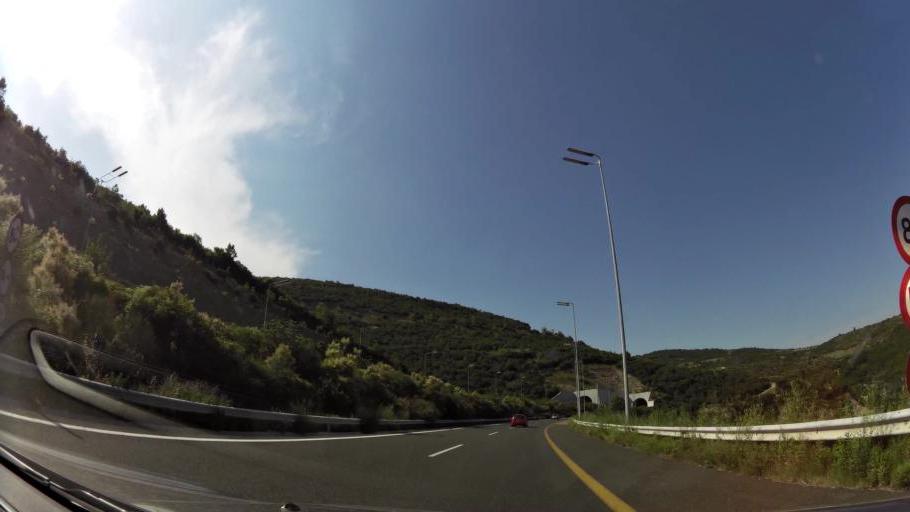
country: GR
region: Central Macedonia
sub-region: Nomos Imathias
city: Rizomata
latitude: 40.4356
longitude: 22.1803
